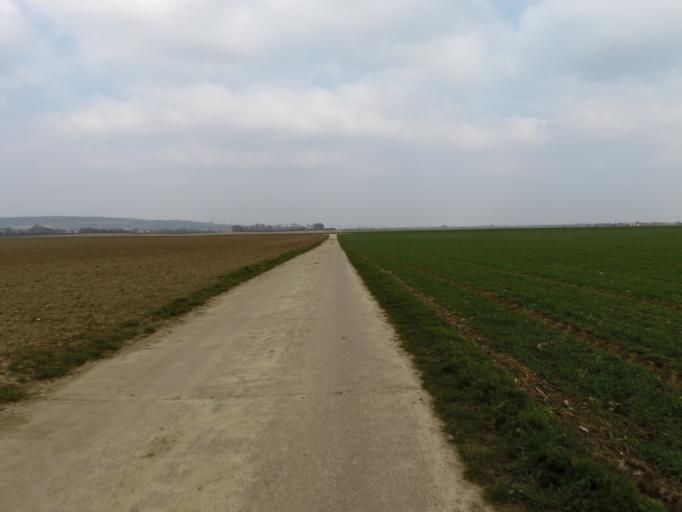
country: DE
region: Rheinland-Pfalz
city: Heidesheim
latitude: 49.5710
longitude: 8.1871
